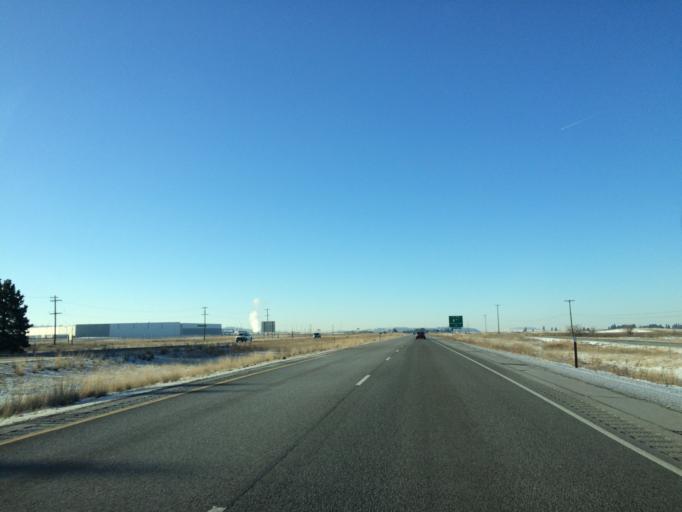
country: US
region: Washington
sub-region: Spokane County
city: Airway Heights
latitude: 47.6023
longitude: -117.5414
